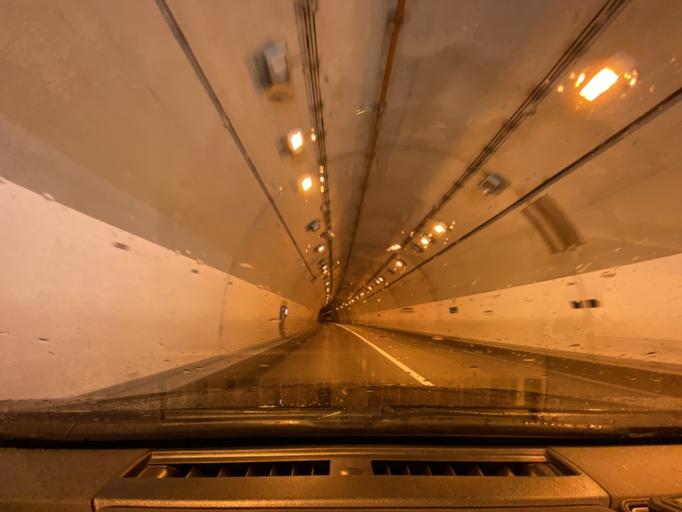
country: JP
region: Hokkaido
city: Rumoi
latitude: 43.6886
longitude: 141.3403
